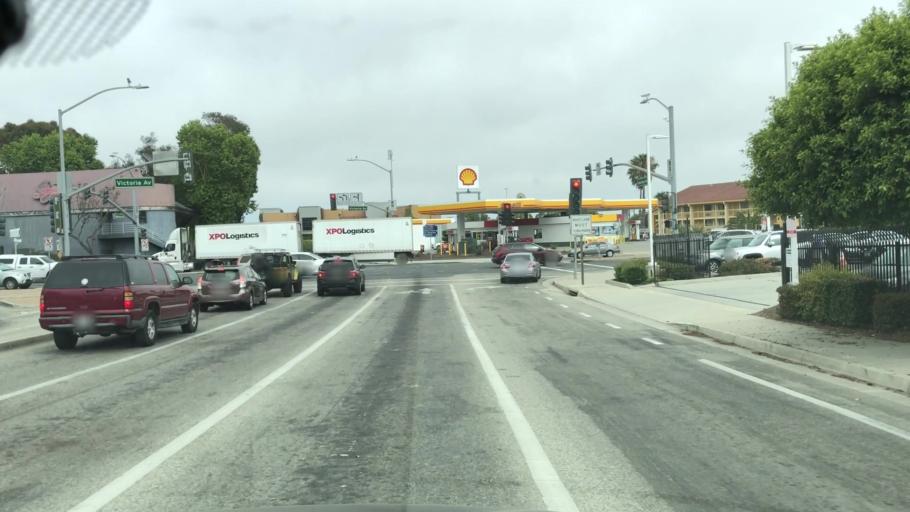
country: US
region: California
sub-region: Ventura County
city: El Rio
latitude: 34.2517
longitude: -119.2124
